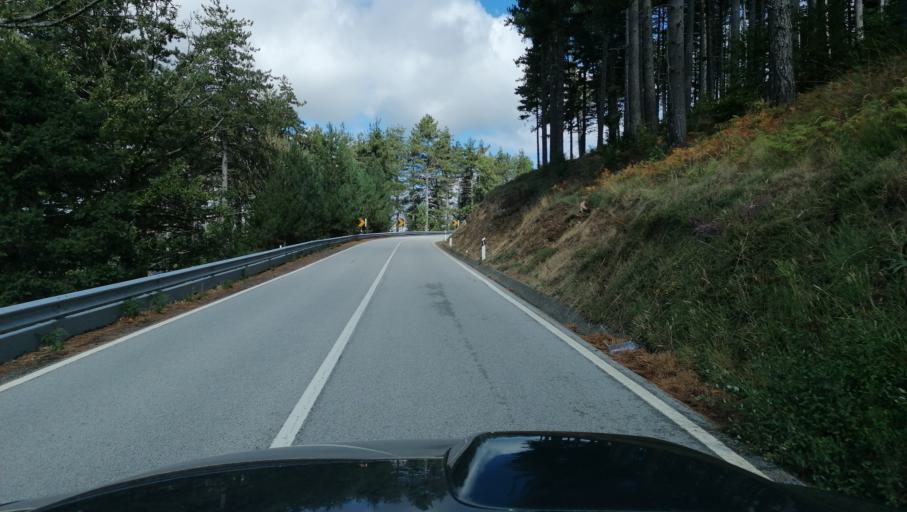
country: PT
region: Vila Real
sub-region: Vila Pouca de Aguiar
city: Vila Pouca de Aguiar
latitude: 41.5078
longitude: -7.6227
